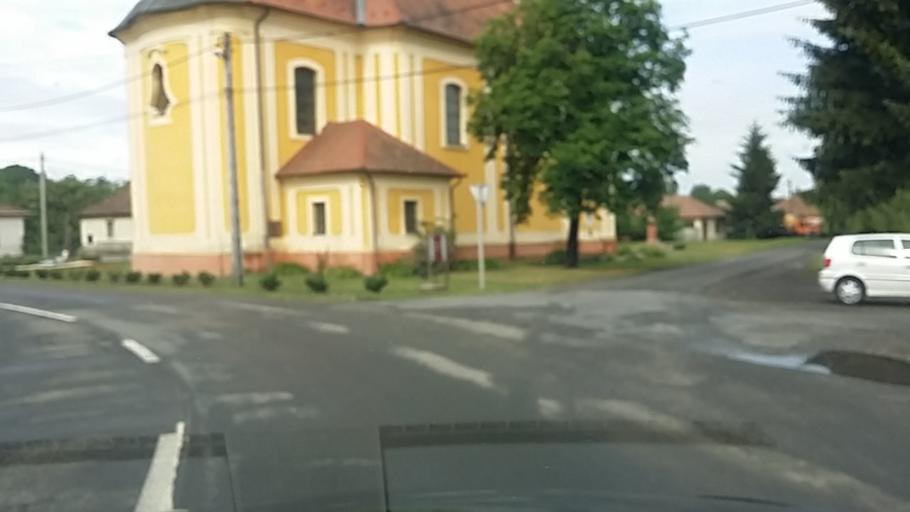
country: SK
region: Nitriansky
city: Zeliezovce
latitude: 47.9777
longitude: 18.7843
